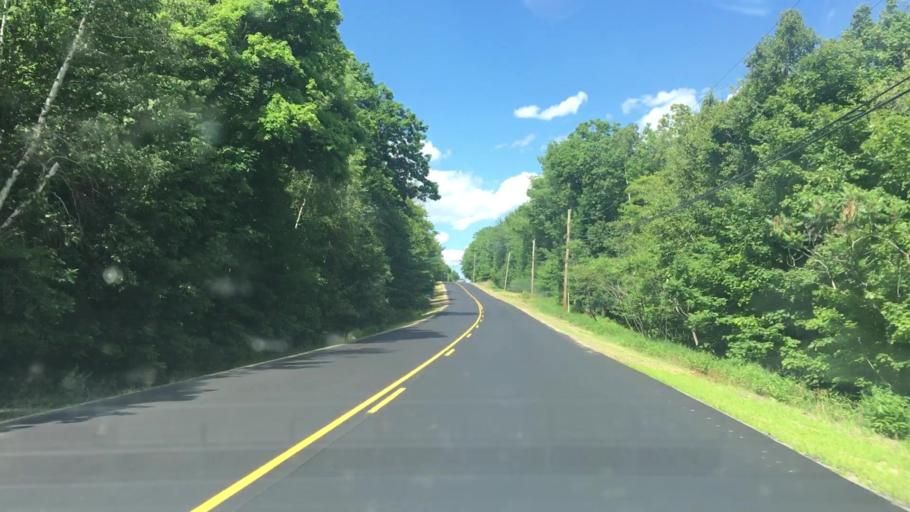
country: US
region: Maine
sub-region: Franklin County
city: Jay
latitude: 44.5489
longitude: -70.1880
